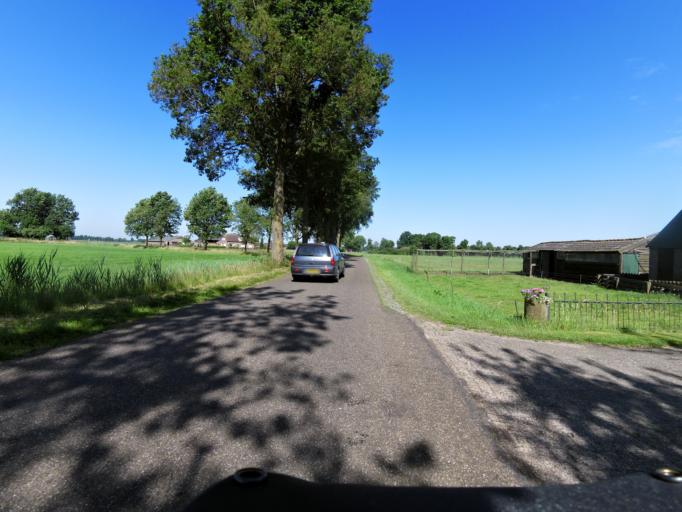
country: NL
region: Overijssel
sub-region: Gemeente Dalfsen
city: Dalfsen
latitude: 52.4773
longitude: 6.3607
